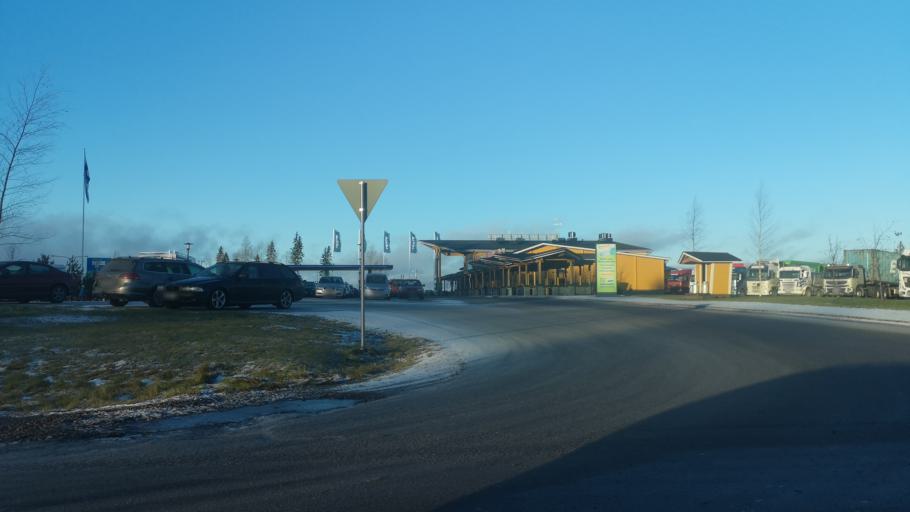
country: FI
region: Paijanne Tavastia
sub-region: Lahti
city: Heinola
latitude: 61.1118
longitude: 25.9294
